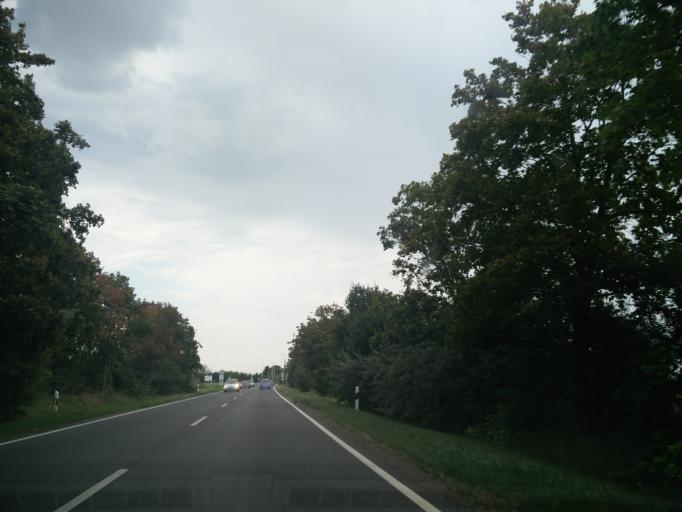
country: HU
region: Fejer
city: Polgardi
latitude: 47.0655
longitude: 18.3100
